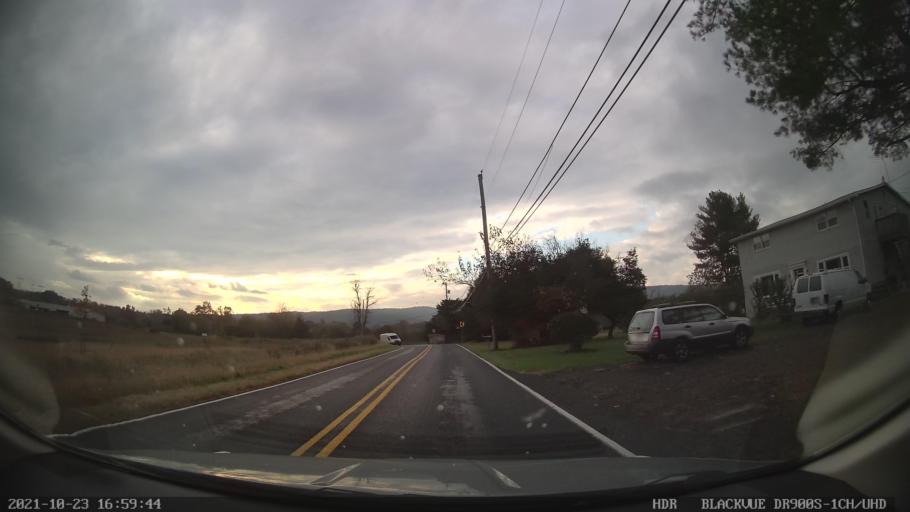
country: US
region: Pennsylvania
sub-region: Berks County
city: Bally
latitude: 40.4286
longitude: -75.5475
